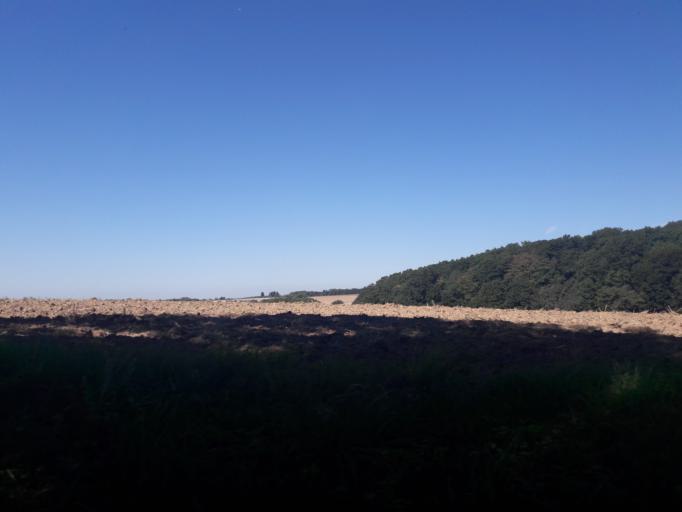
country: DE
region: Baden-Wuerttemberg
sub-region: Karlsruhe Region
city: Ubstadt-Weiher
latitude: 49.1294
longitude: 8.6507
